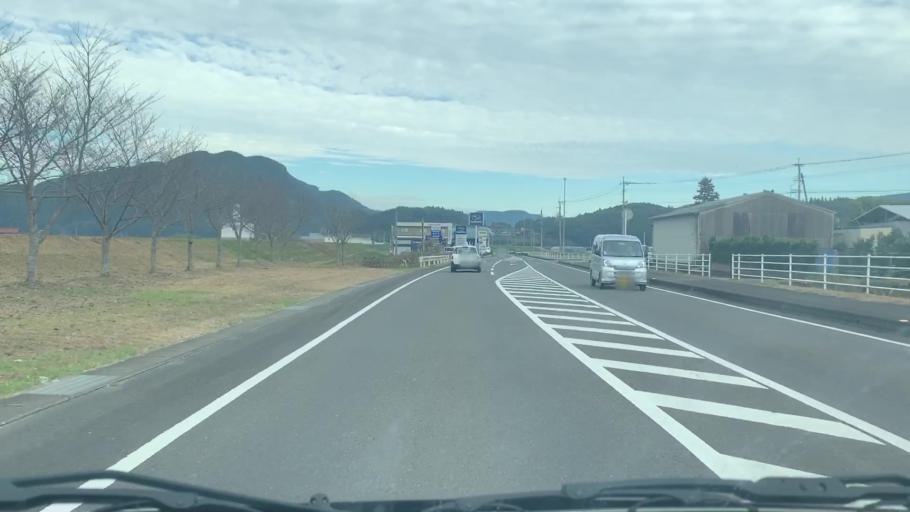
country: JP
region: Saga Prefecture
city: Imaricho-ko
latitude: 33.2947
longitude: 129.9699
